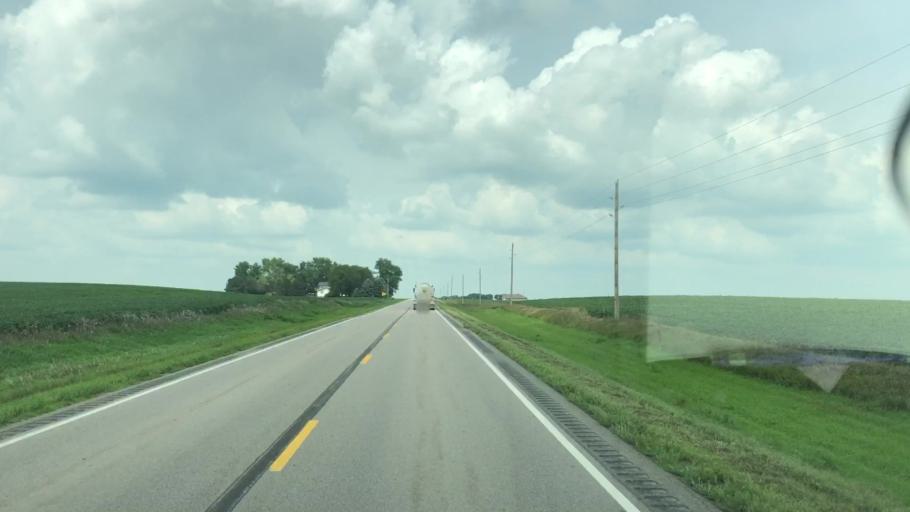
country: US
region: Iowa
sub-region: Plymouth County
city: Remsen
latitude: 42.7872
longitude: -95.9578
